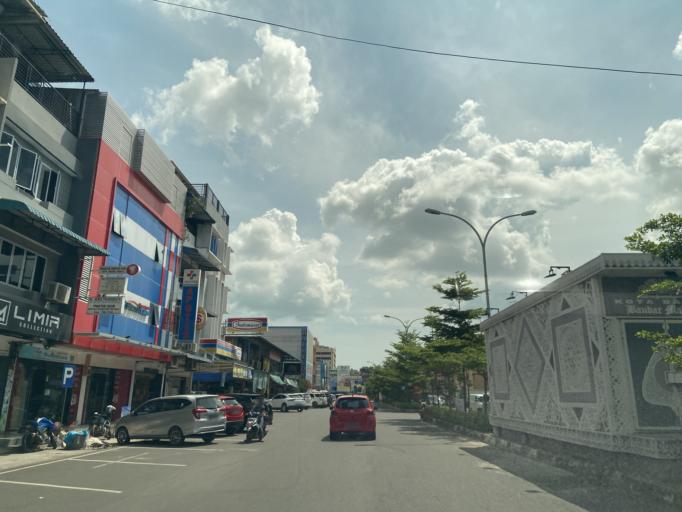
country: SG
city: Singapore
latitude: 1.1464
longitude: 104.0081
